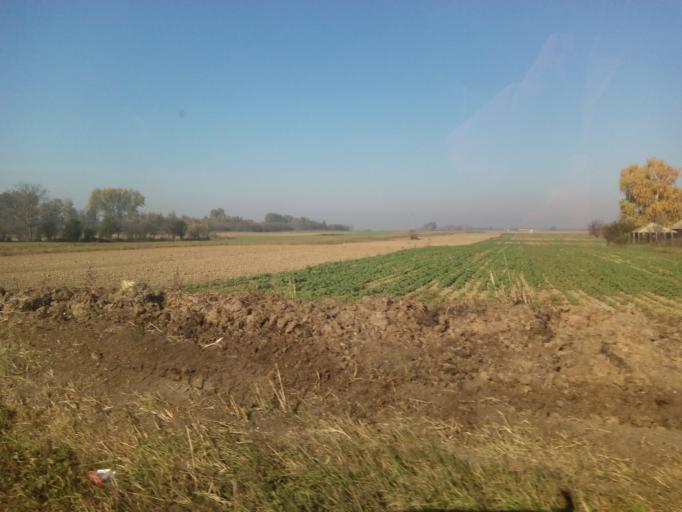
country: RS
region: Autonomna Pokrajina Vojvodina
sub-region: Juznobacki Okrug
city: Backa Palanka
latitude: 45.2492
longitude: 19.4539
